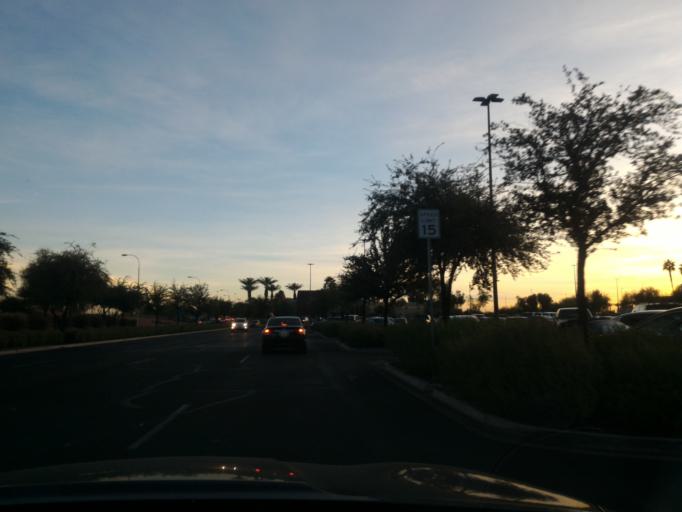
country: US
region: Arizona
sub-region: Maricopa County
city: Chandler
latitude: 33.3016
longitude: -111.8953
